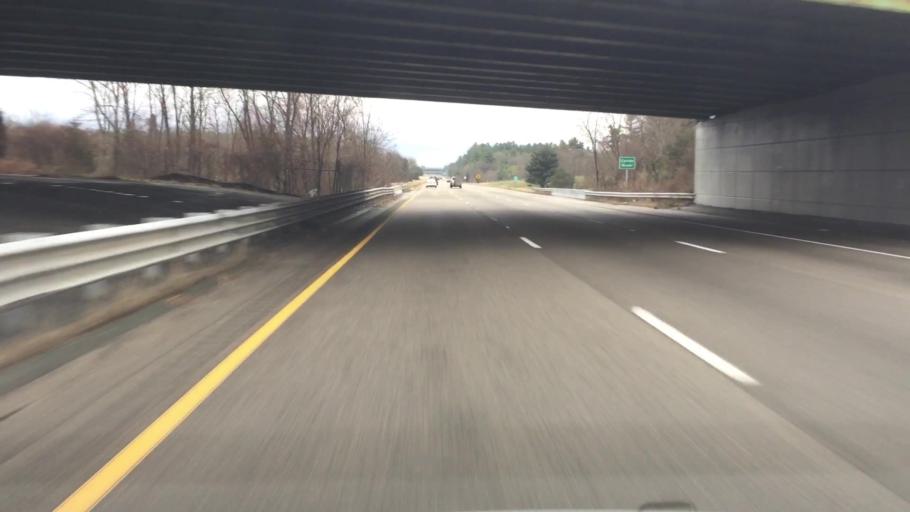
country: US
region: Massachusetts
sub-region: Bristol County
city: Norton Center
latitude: 41.9823
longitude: -71.1598
